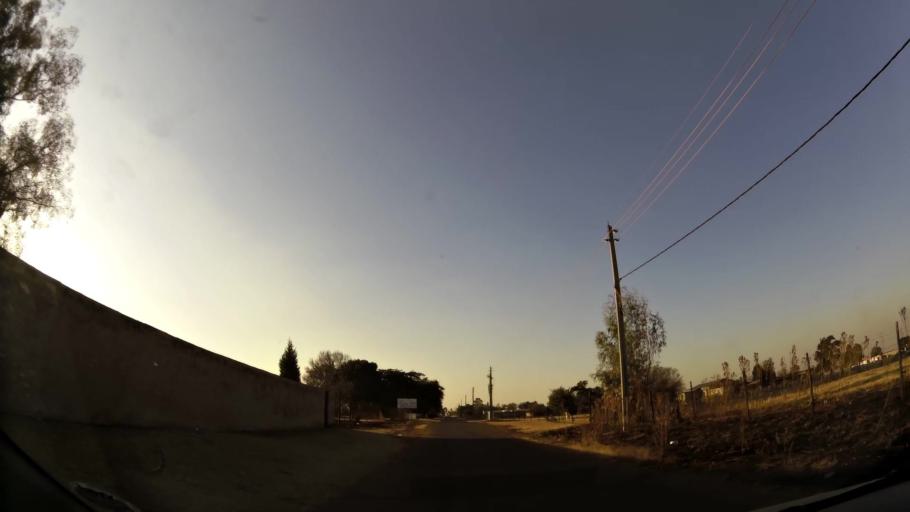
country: ZA
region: Gauteng
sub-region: West Rand District Municipality
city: Randfontein
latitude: -26.2062
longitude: 27.6444
